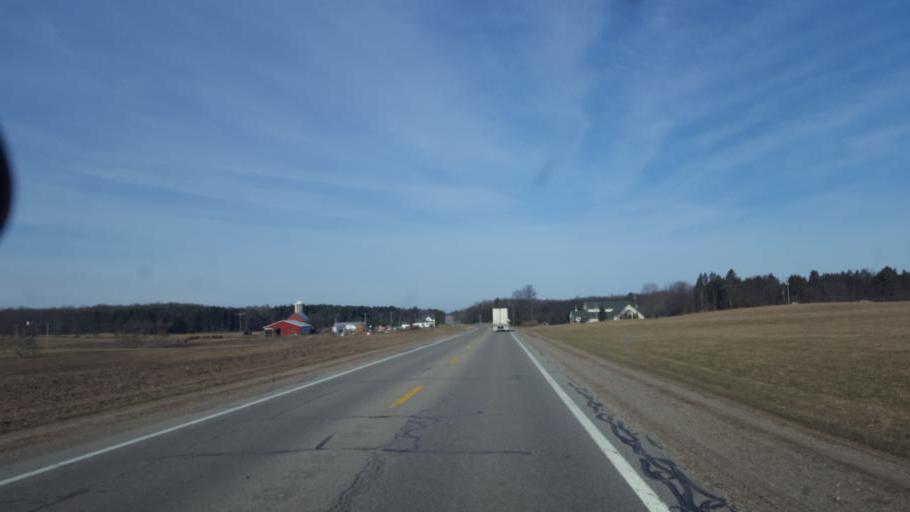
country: US
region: Michigan
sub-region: Montcalm County
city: Lakeview
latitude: 43.4307
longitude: -85.2104
